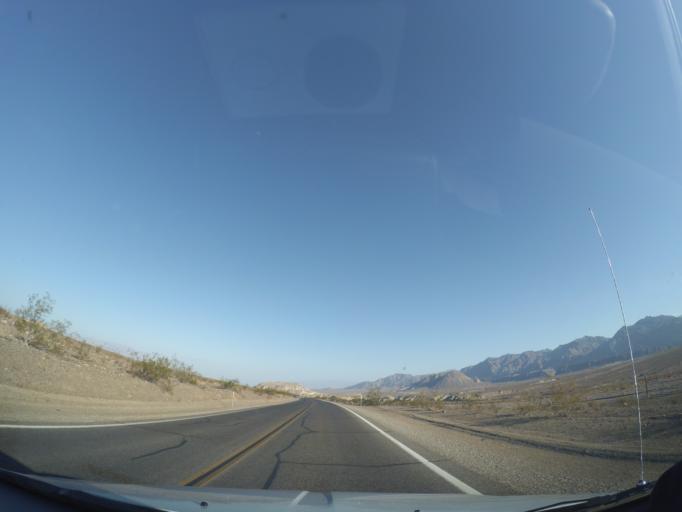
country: US
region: Nevada
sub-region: Nye County
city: Beatty
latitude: 36.3735
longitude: -116.7332
